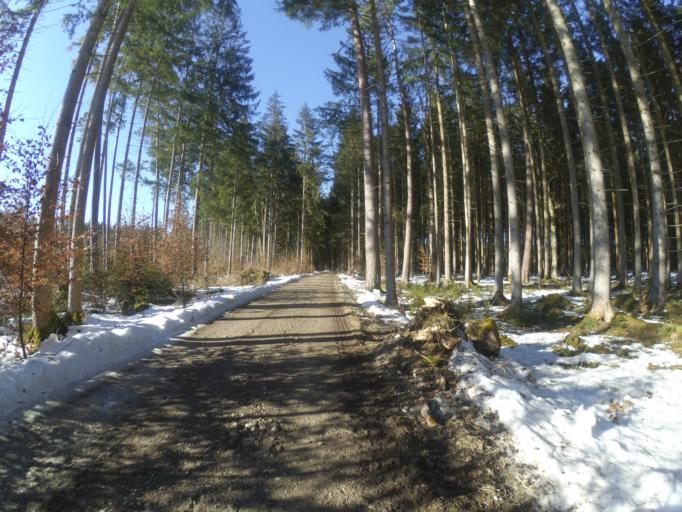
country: DE
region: Bavaria
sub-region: Upper Bavaria
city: Aying
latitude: 47.9847
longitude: 11.7563
